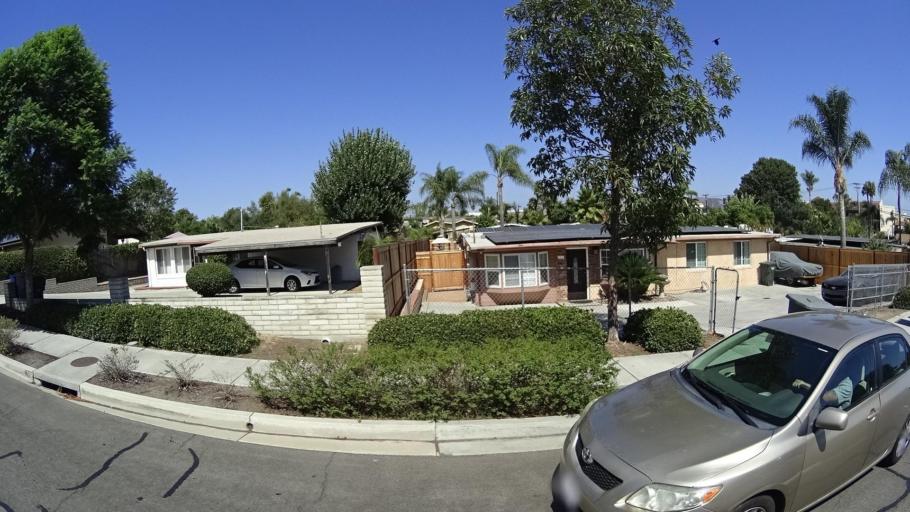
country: US
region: California
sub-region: San Diego County
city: Lake San Marcos
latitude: 33.1407
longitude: -117.2043
